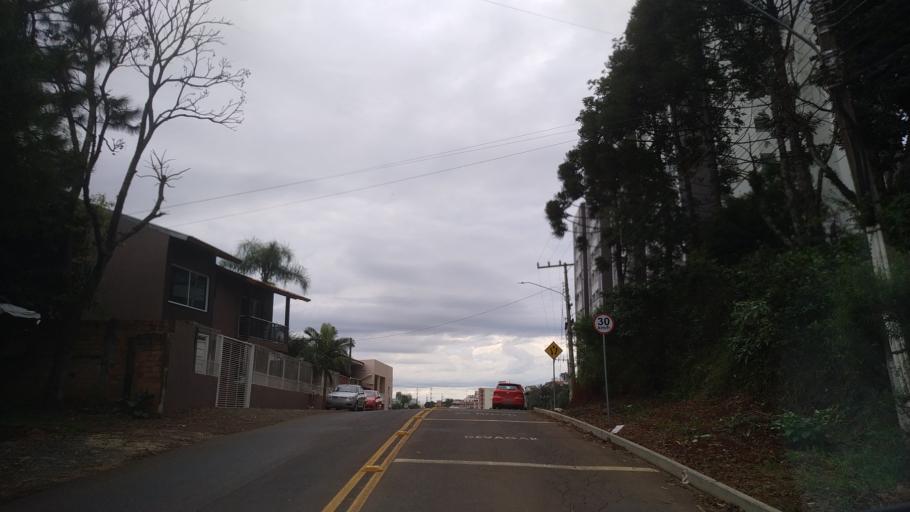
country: BR
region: Santa Catarina
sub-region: Chapeco
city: Chapeco
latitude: -27.0733
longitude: -52.6085
